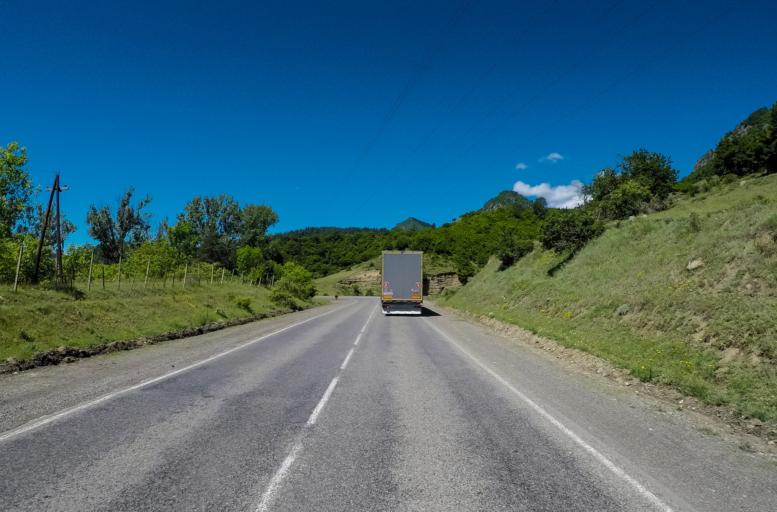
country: GE
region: Samtskhe-Javakheti
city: Borjomi
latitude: 41.7812
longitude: 43.2555
